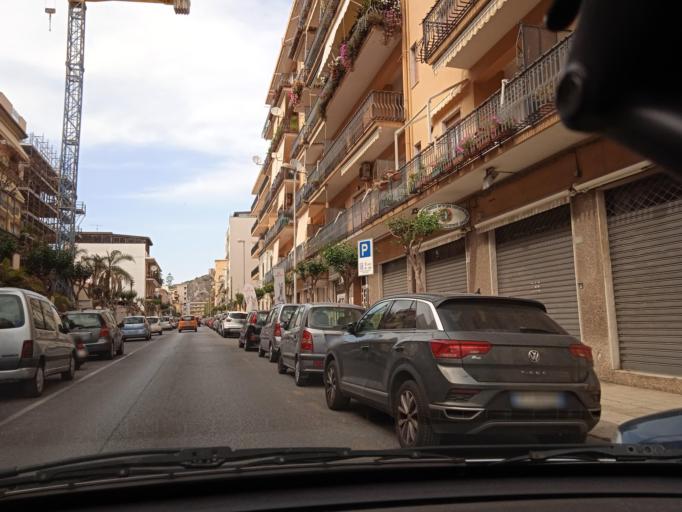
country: IT
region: Sicily
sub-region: Messina
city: Milazzo
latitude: 38.2218
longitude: 15.2392
